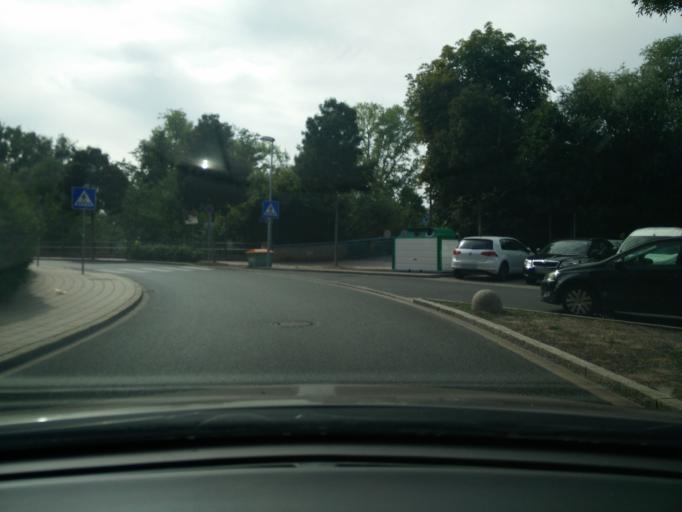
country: DE
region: Bavaria
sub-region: Regierungsbezirk Mittelfranken
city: Furth
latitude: 49.4766
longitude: 10.9811
